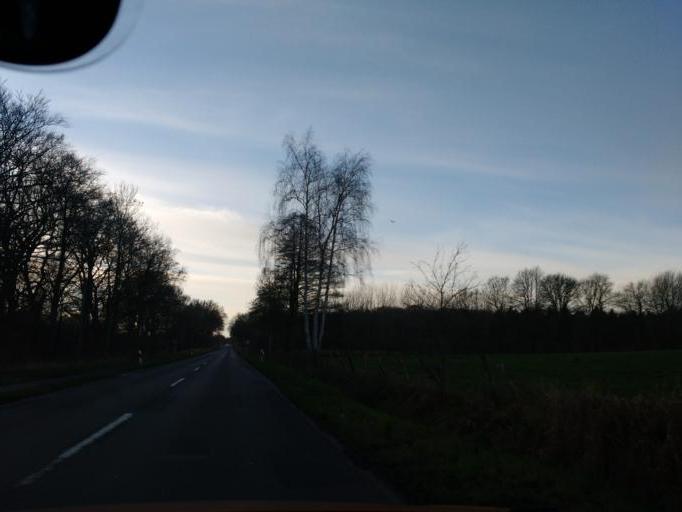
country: DE
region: Lower Saxony
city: Hude
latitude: 53.1148
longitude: 8.4443
